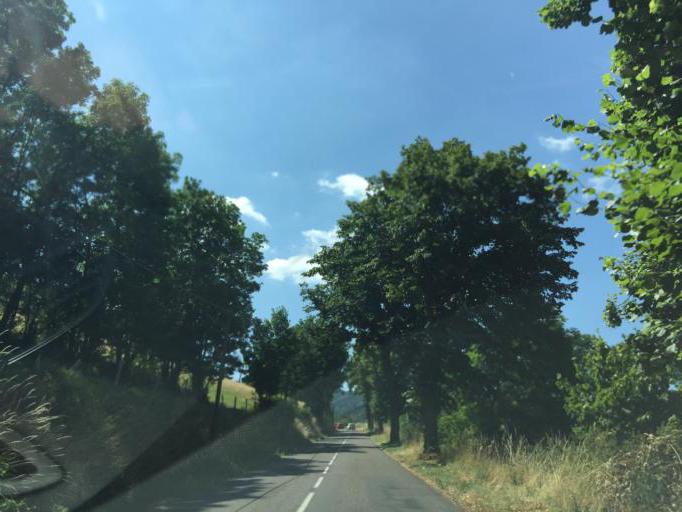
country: FR
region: Rhone-Alpes
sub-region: Departement de la Loire
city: Saint-Chamond
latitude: 45.4213
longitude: 4.5155
